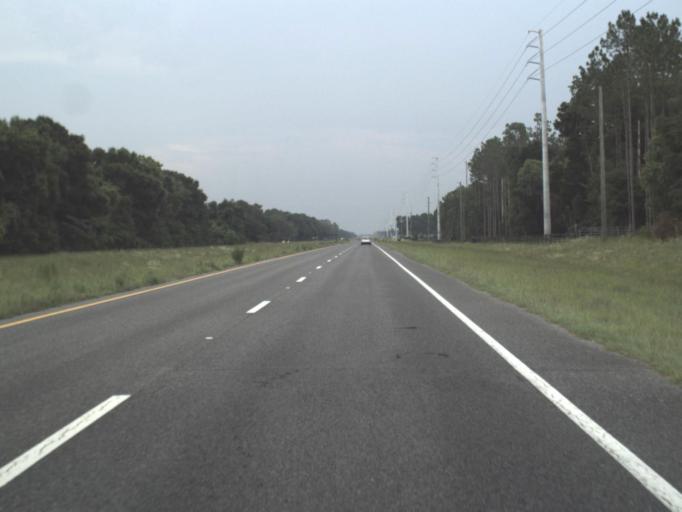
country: US
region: Florida
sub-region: Levy County
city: Chiefland
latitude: 29.4748
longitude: -82.7955
